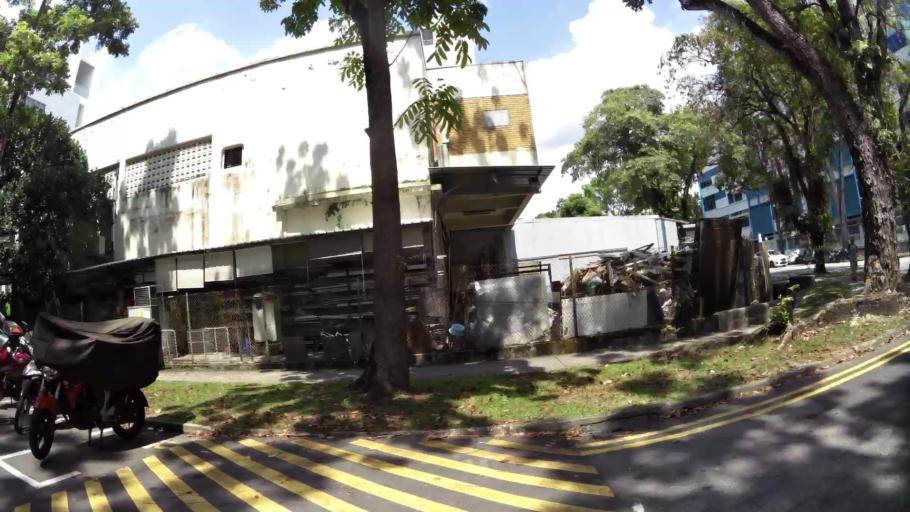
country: SG
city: Singapore
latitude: 1.3830
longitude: 103.8280
